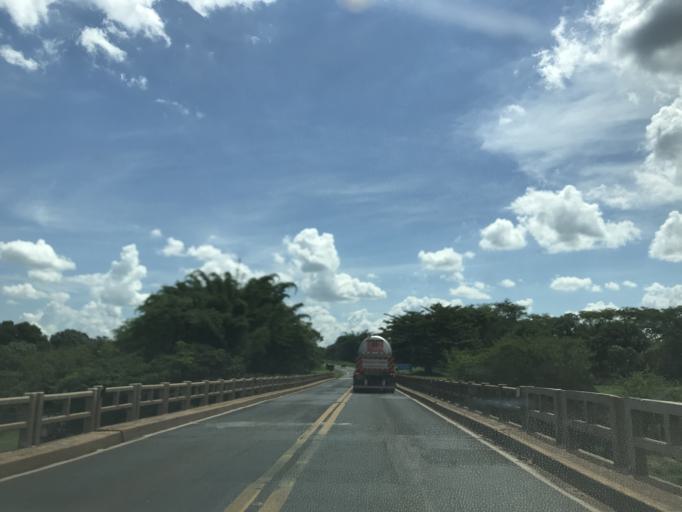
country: BR
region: Sao Paulo
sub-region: Nova Granada
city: Nova Granada
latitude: -20.4186
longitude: -49.2667
